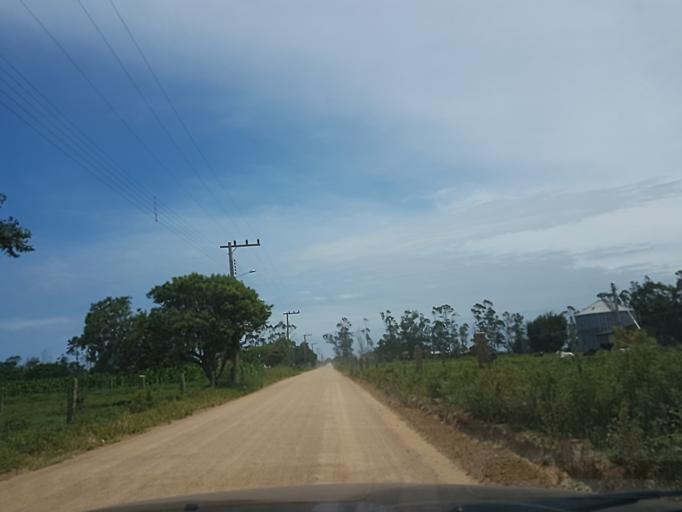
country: BR
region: Santa Catarina
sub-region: Jaguaruna
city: Jaguaruna
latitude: -28.6356
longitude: -48.9580
